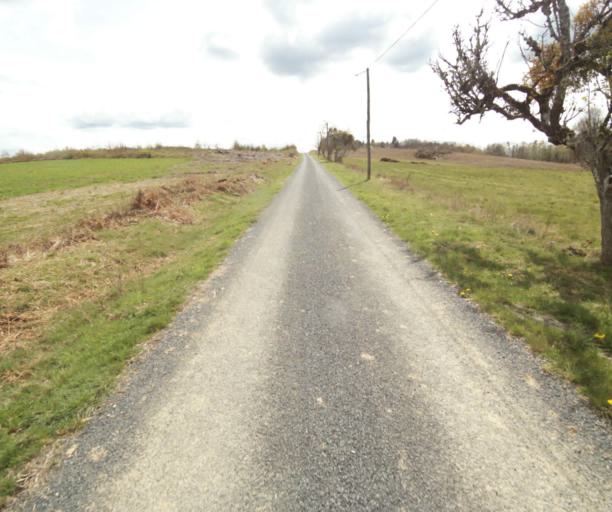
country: FR
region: Limousin
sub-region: Departement de la Correze
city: Laguenne
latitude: 45.2366
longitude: 1.8726
